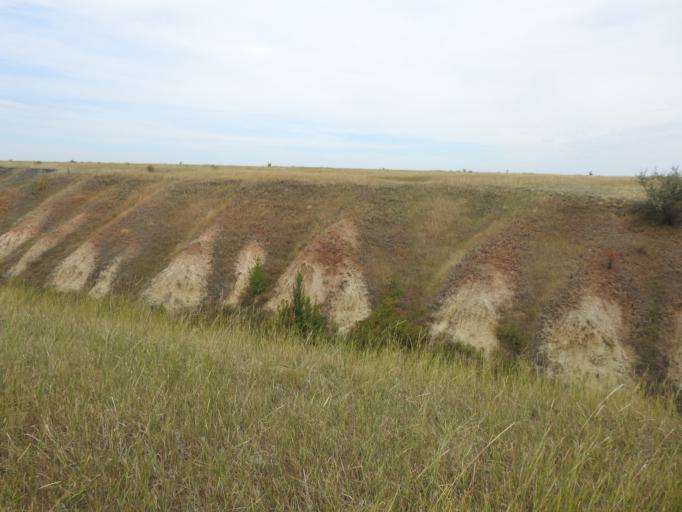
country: RU
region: Volgograd
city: Zhirnovsk
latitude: 51.2058
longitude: 44.9350
